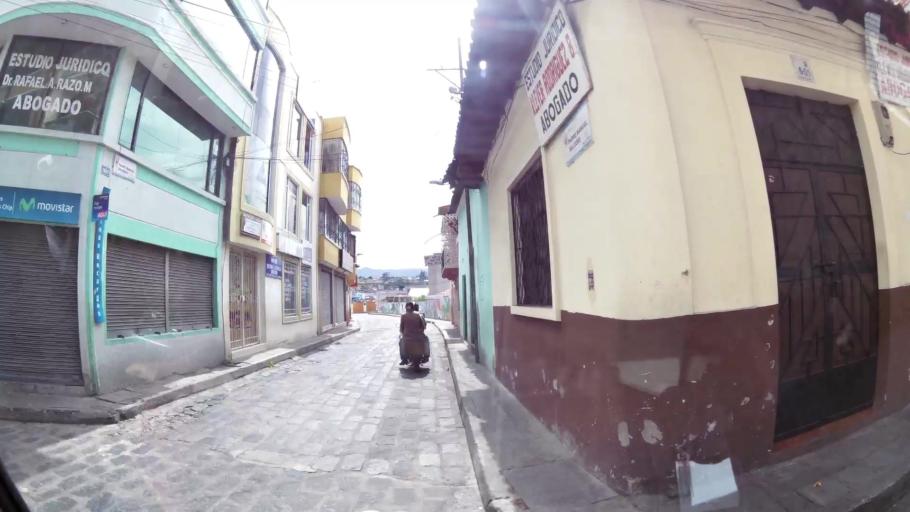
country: EC
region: Cotopaxi
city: Latacunga
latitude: -0.9337
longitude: -78.6171
